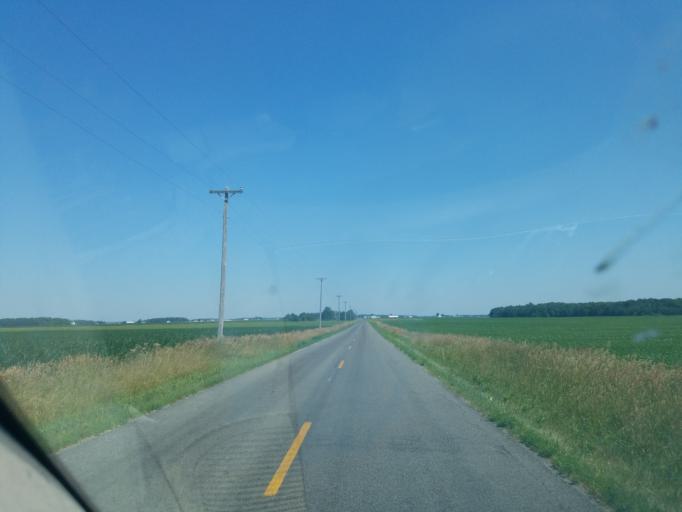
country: US
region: Ohio
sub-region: Mercer County
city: Rockford
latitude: 40.6355
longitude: -84.7087
